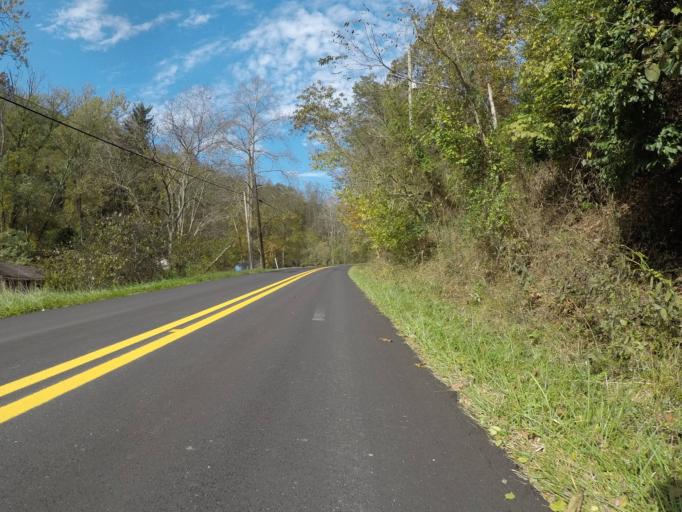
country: US
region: West Virginia
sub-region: Wayne County
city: Lavalette
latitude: 38.3635
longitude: -82.4293
